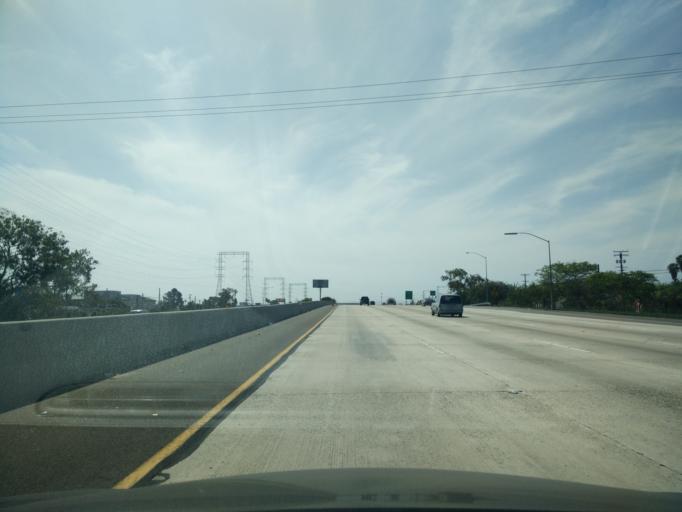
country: US
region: California
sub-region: San Diego County
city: National City
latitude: 32.6630
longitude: -117.1092
